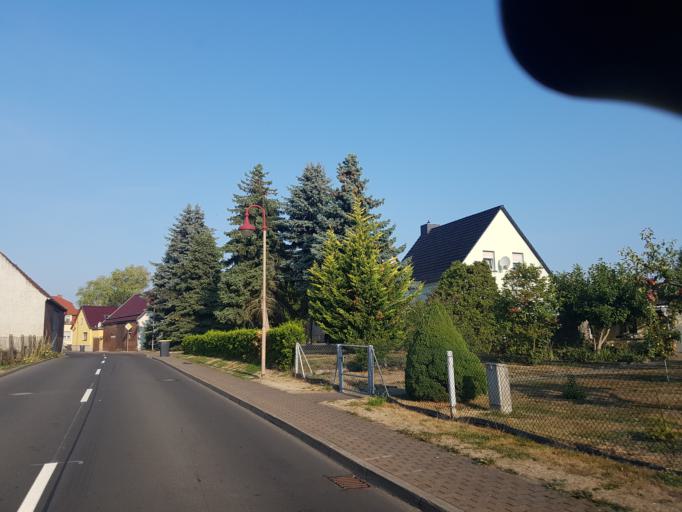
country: DE
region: Saxony-Anhalt
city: Nudersdorf
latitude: 51.9671
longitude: 12.5714
